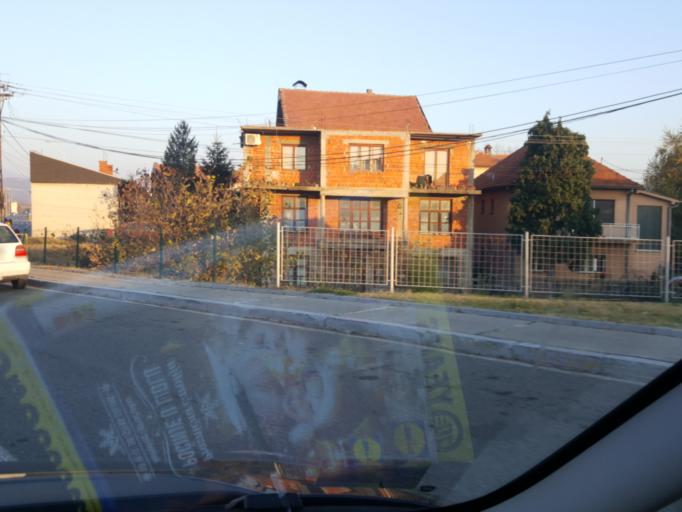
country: RS
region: Central Serbia
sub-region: Nisavski Okrug
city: Nis
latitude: 43.3298
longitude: 21.9415
